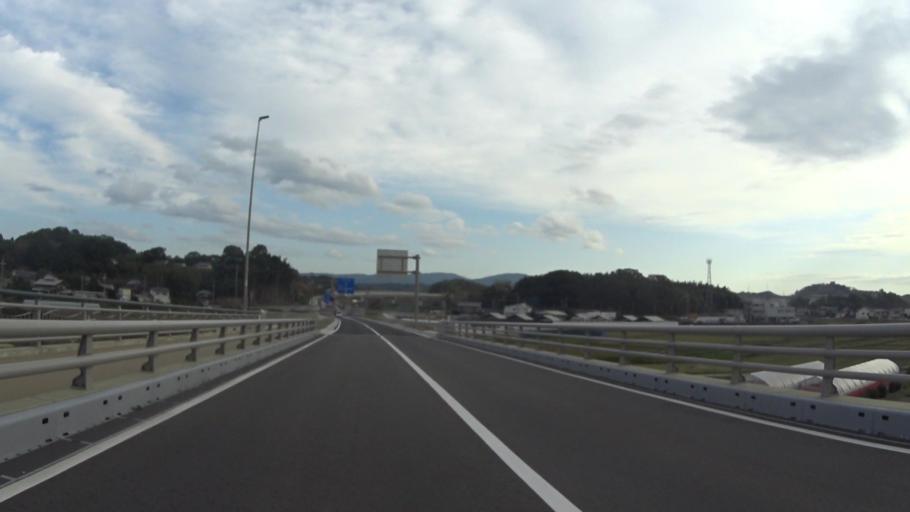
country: JP
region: Nara
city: Nara-shi
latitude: 34.7466
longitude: 135.8317
